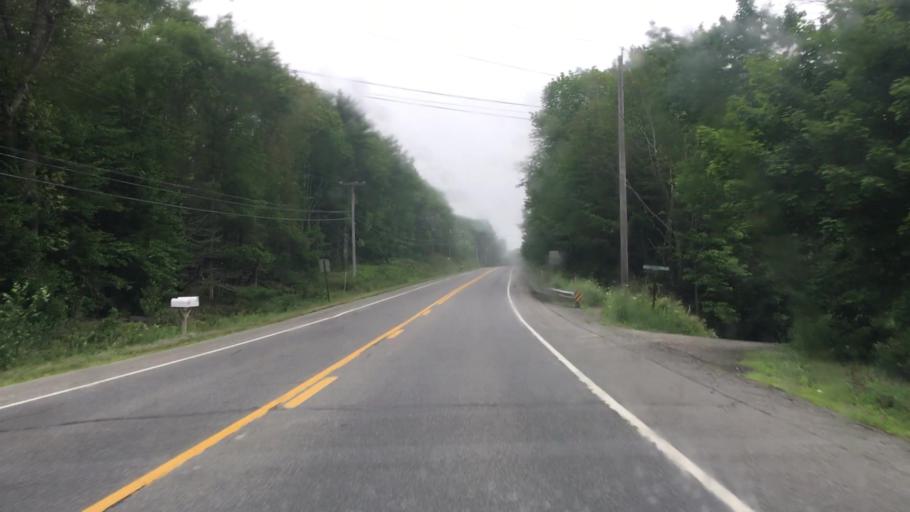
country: US
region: Maine
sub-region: Lincoln County
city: Wiscasset
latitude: 44.0265
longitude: -69.6711
